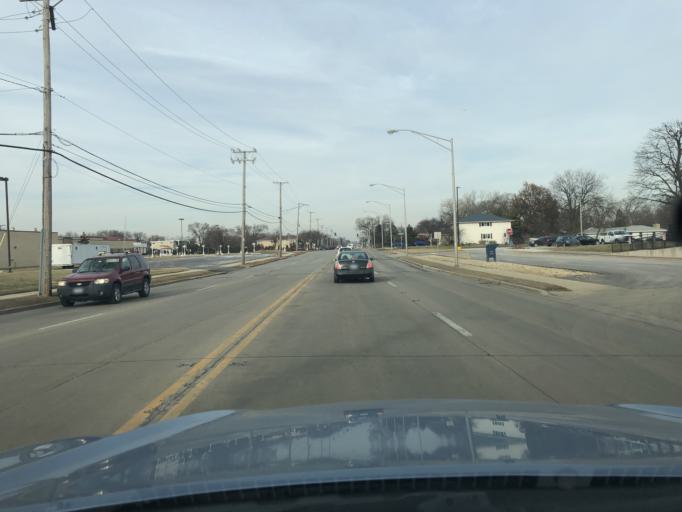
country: US
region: Illinois
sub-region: DuPage County
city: Addison
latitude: 41.9335
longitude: -87.9887
